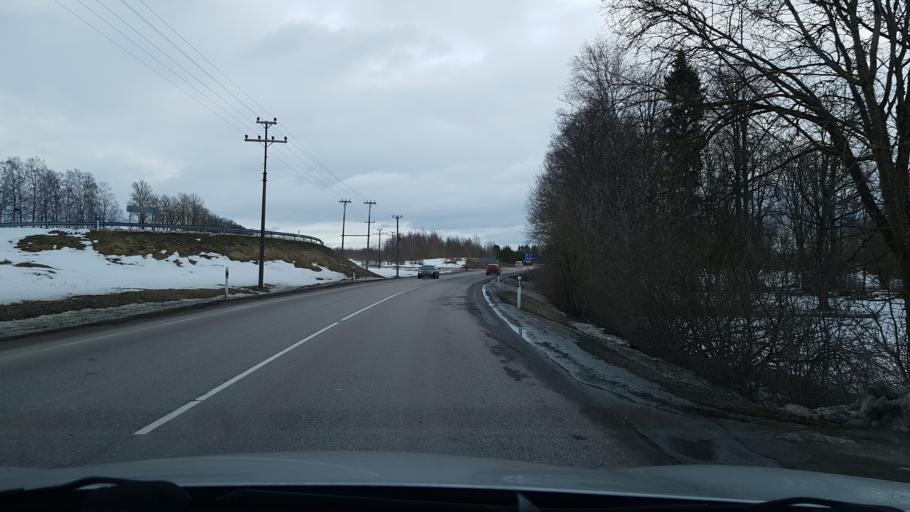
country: EE
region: Jogevamaa
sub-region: Jogeva linn
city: Jogeva
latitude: 58.6908
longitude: 26.4585
